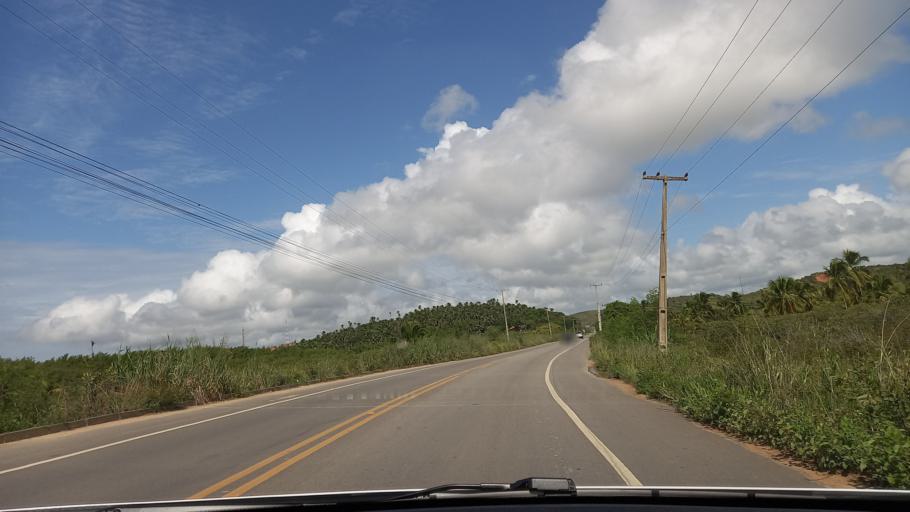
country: BR
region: Alagoas
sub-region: Maragogi
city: Maragogi
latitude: -8.9952
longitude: -35.2093
